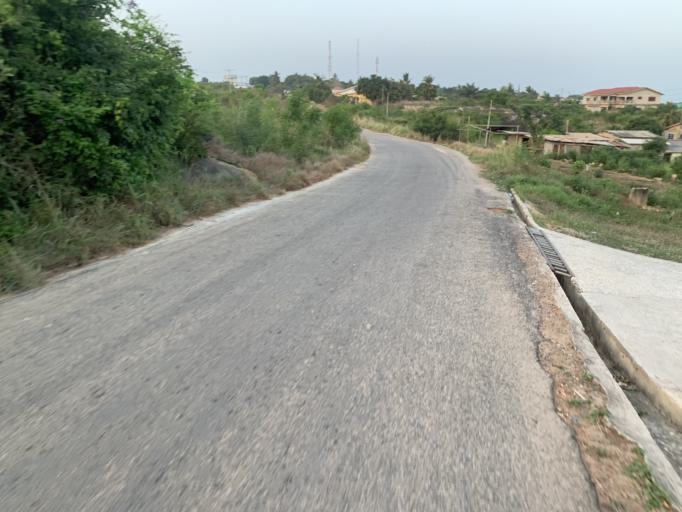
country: GH
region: Central
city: Winneba
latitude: 5.3617
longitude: -0.6221
